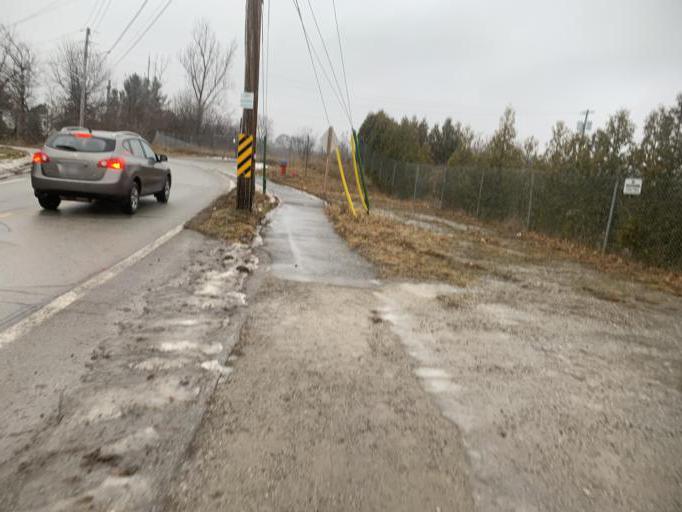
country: CA
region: Ontario
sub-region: Halton
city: Milton
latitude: 43.6583
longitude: -79.9256
